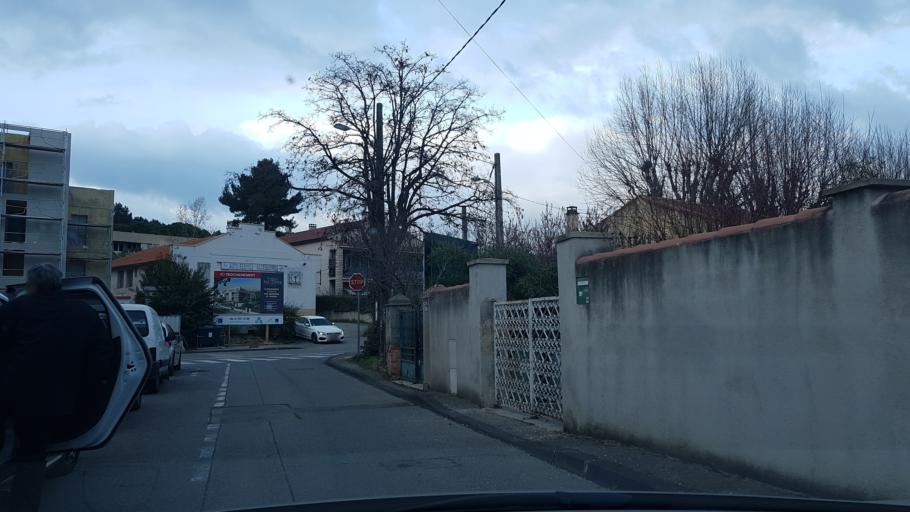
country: FR
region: Provence-Alpes-Cote d'Azur
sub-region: Departement des Bouches-du-Rhone
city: Gardanne
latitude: 43.4586
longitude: 5.4760
